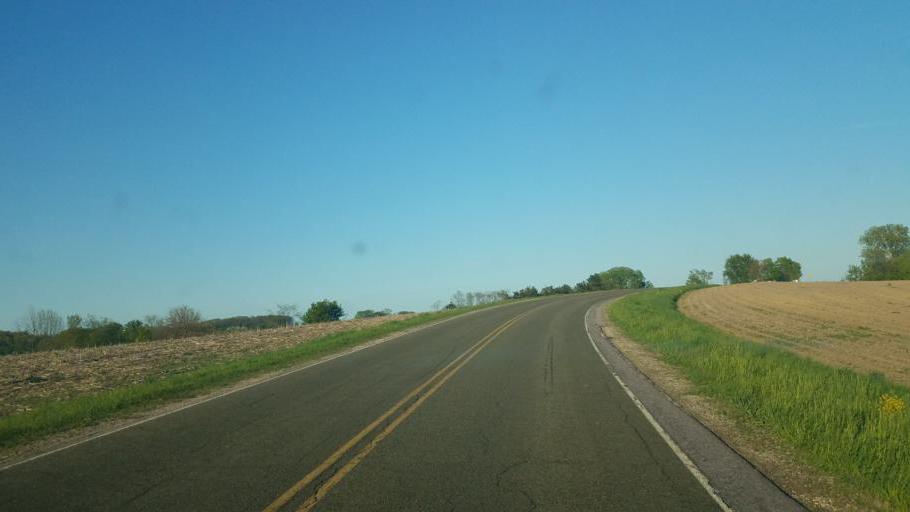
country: US
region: Wisconsin
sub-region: Vernon County
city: Hillsboro
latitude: 43.6437
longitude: -90.2782
